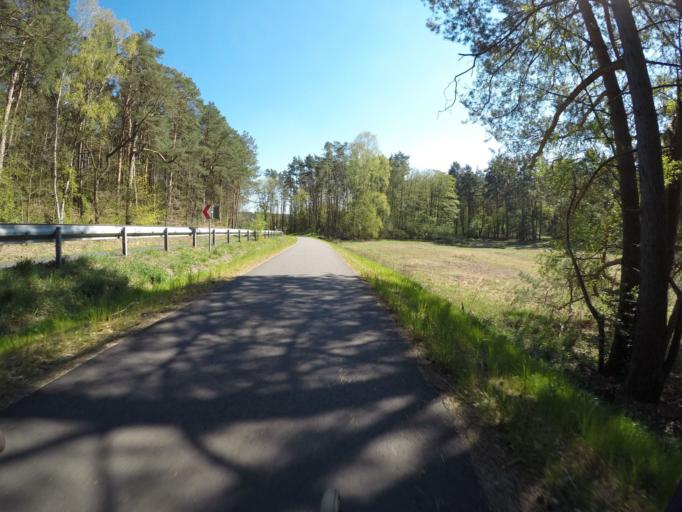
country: DE
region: Brandenburg
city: Strausberg
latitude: 52.5983
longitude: 13.8877
